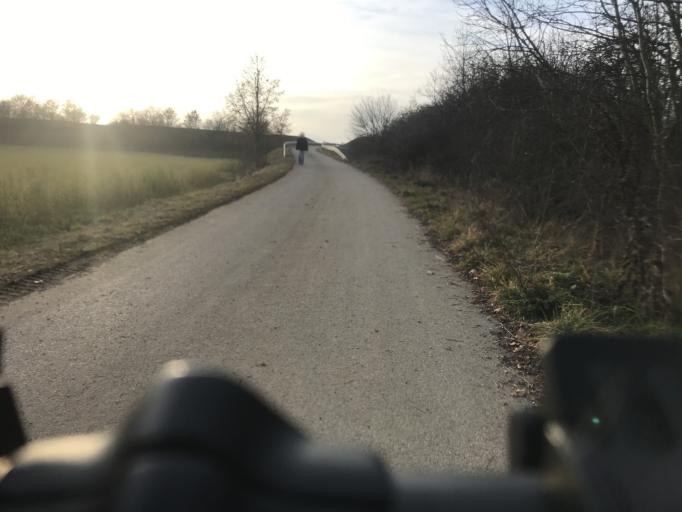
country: DE
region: Bavaria
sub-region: Upper Bavaria
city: Germering
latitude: 48.1429
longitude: 11.3975
